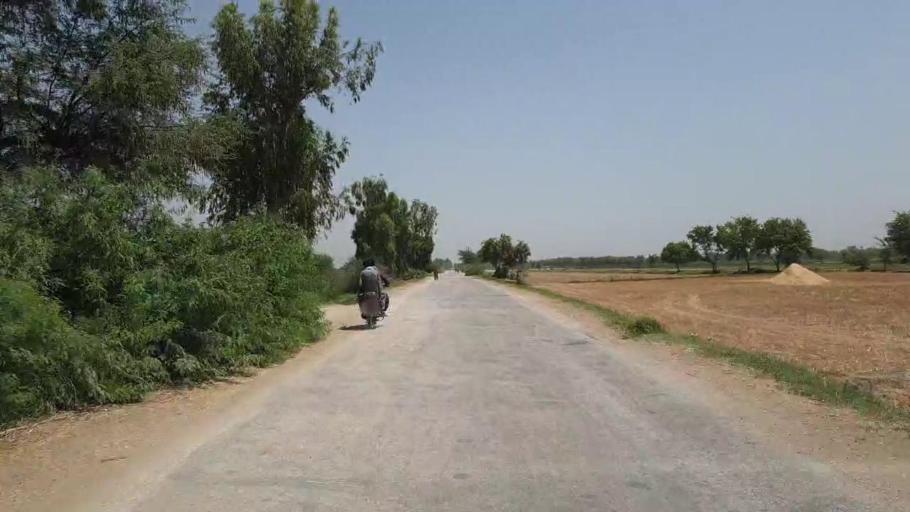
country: PK
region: Sindh
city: Adilpur
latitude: 27.9026
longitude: 69.2945
